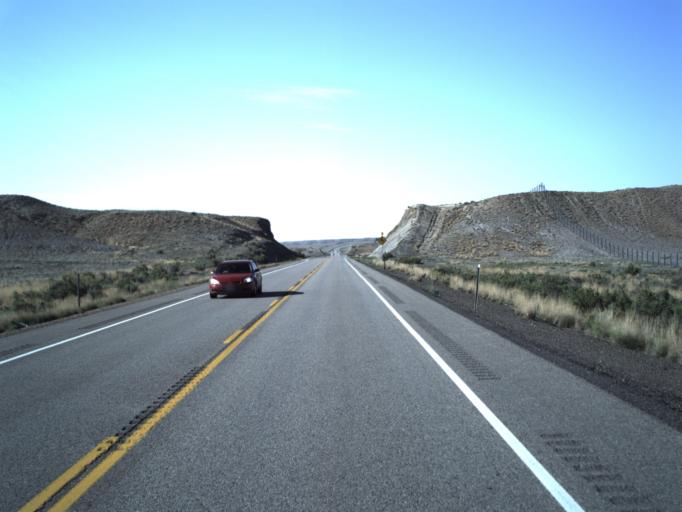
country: US
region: Utah
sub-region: Emery County
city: Huntington
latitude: 39.4479
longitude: -110.8634
